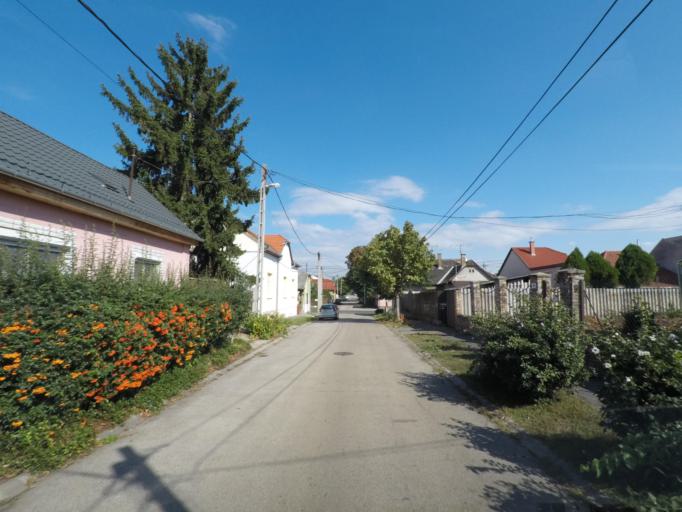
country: HU
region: Budapest
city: Budapest XX. keruelet
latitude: 47.4224
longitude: 19.1171
